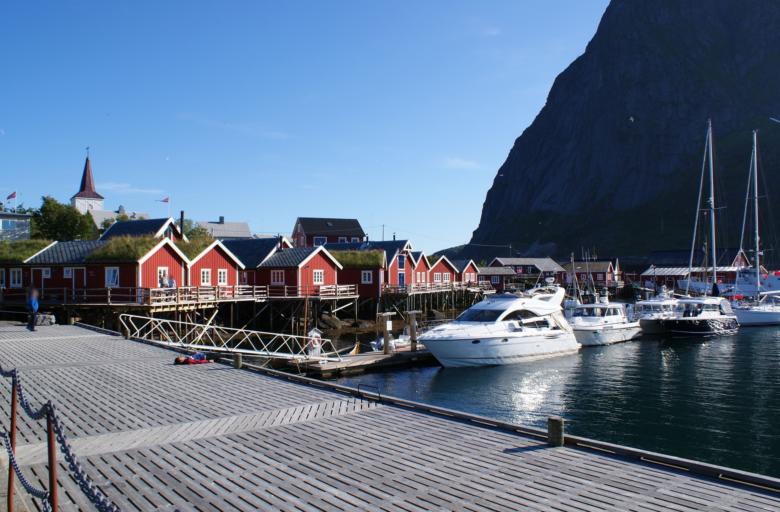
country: NO
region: Nordland
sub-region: Moskenes
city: Reine
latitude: 67.9346
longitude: 13.0876
